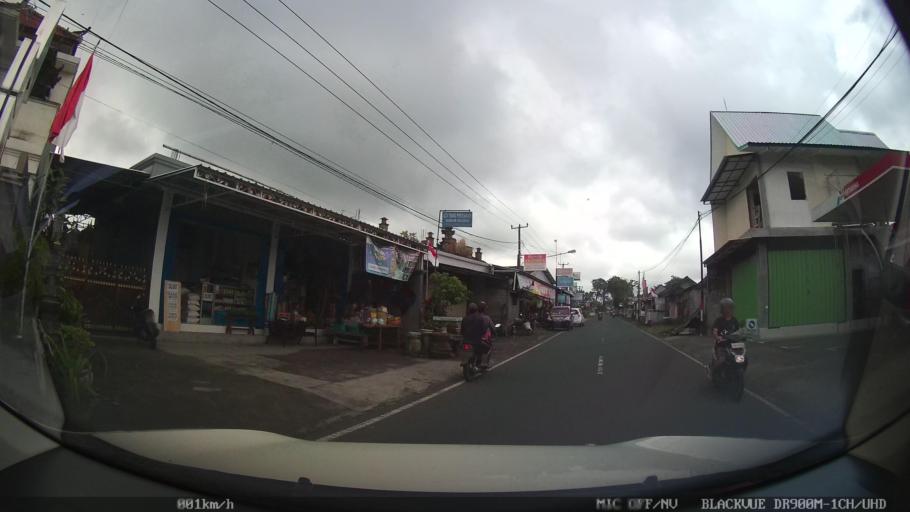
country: ID
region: Bali
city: Petang
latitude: -8.4054
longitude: 115.2194
